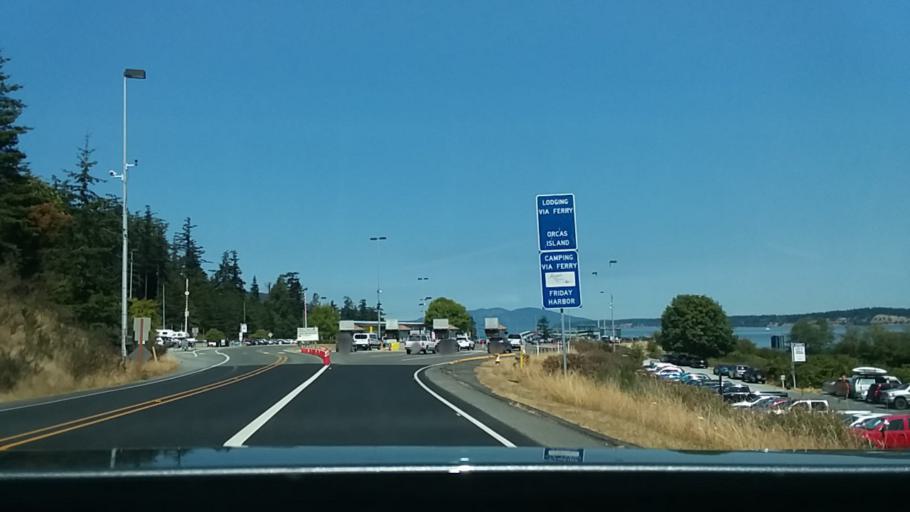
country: US
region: Washington
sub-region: Skagit County
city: Anacortes
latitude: 48.5022
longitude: -122.6793
